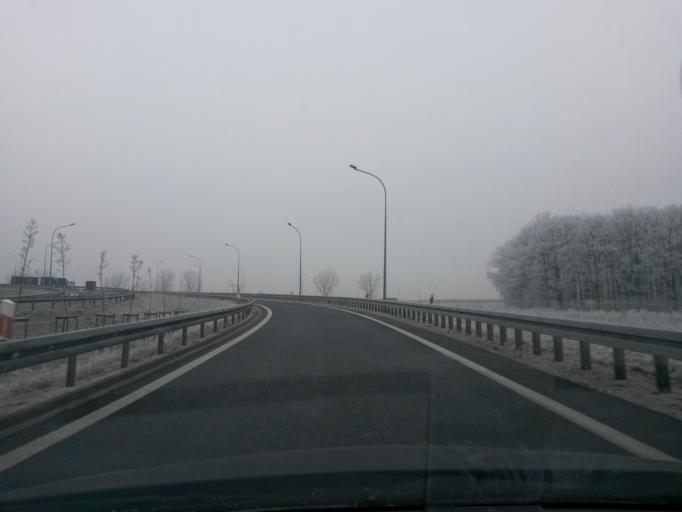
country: PL
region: Greater Poland Voivodeship
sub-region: Powiat poznanski
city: Kostrzyn
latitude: 52.3967
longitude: 17.2599
